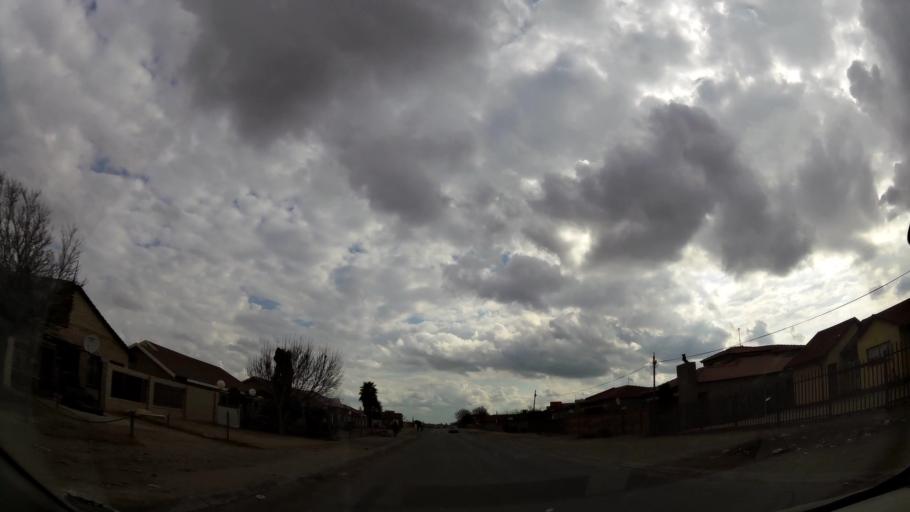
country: ZA
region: Orange Free State
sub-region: Fezile Dabi District Municipality
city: Sasolburg
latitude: -26.8495
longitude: 27.8579
